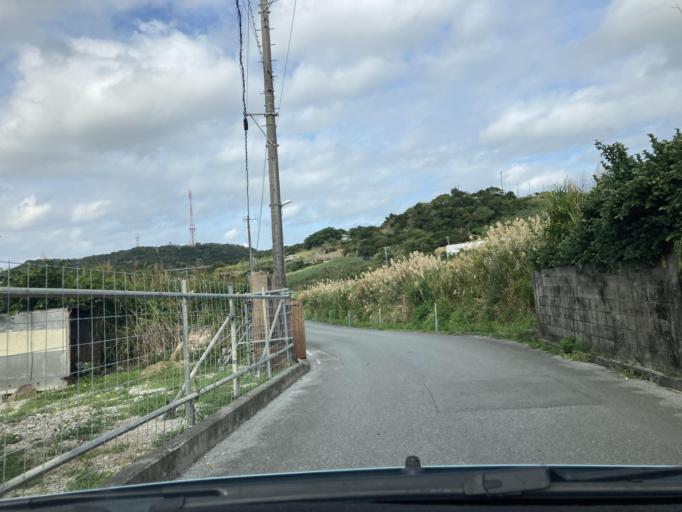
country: JP
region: Okinawa
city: Ginowan
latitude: 26.2108
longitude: 127.7455
